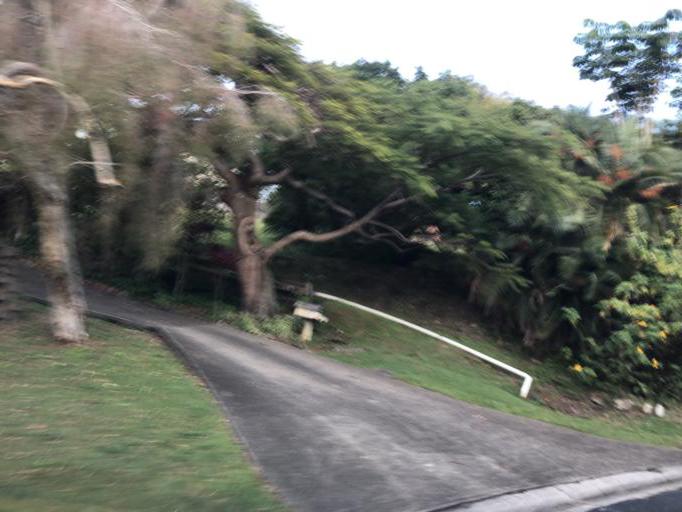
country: AU
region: New South Wales
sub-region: Coffs Harbour
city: Coffs Harbour
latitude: -30.3086
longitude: 153.1335
